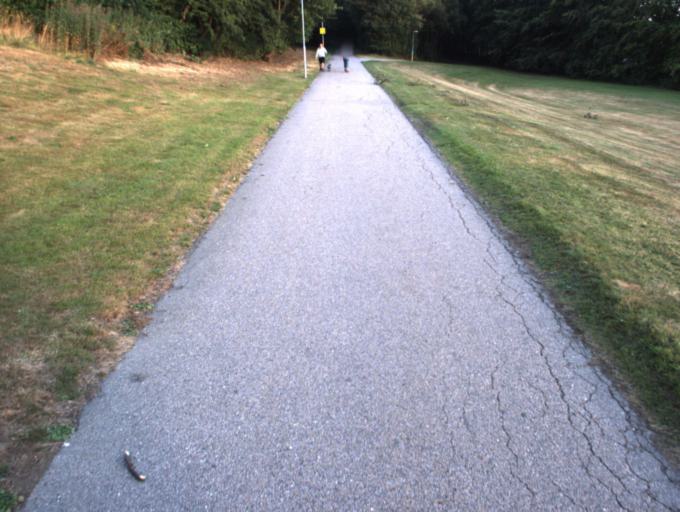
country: SE
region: Skane
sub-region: Helsingborg
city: Helsingborg
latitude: 56.0287
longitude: 12.7232
